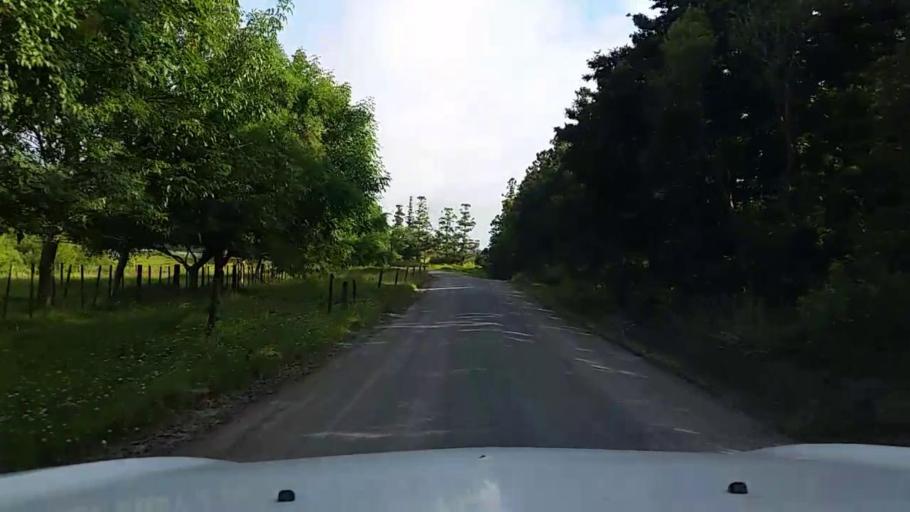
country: NZ
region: Northland
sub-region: Whangarei
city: Maungatapere
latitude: -35.6796
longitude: 174.1785
